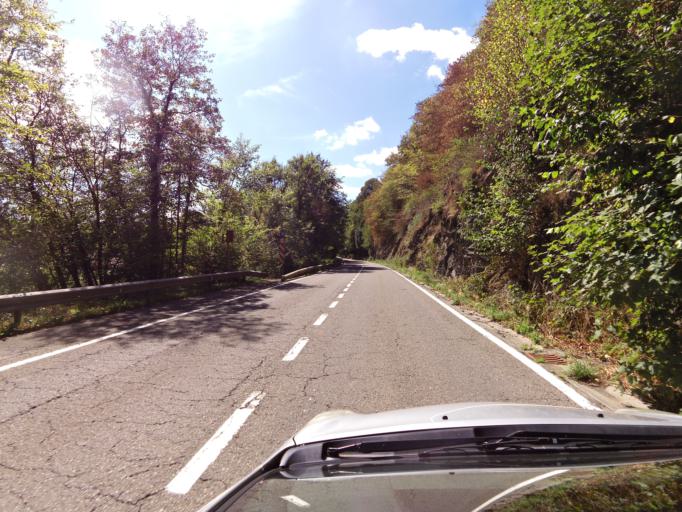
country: BE
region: Wallonia
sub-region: Province du Luxembourg
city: Rendeux
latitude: 50.2214
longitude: 5.5208
